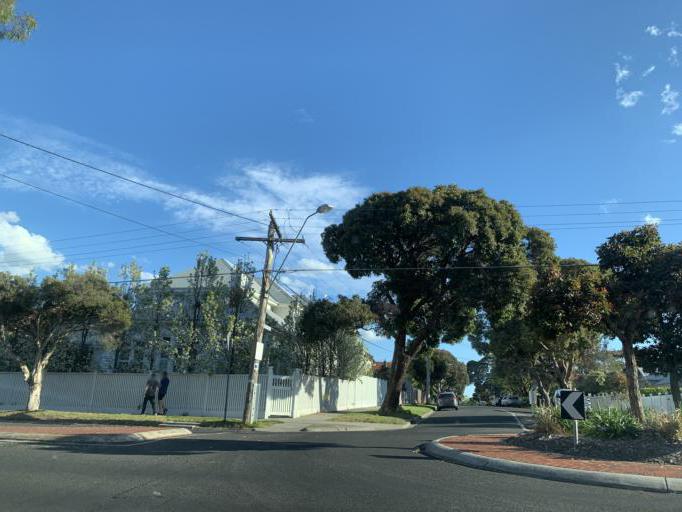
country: AU
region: Victoria
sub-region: Bayside
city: Hampton
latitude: -37.9403
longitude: 145.0101
